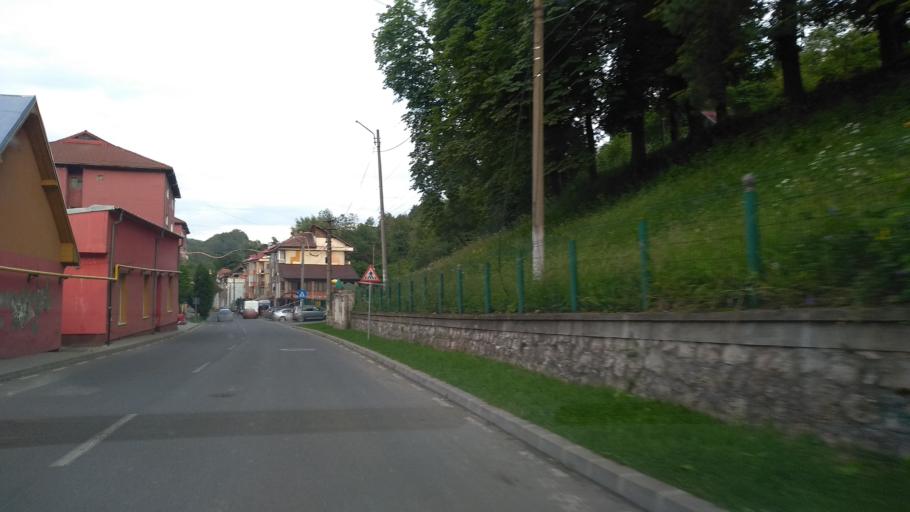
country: RO
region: Hunedoara
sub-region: Comuna Aninoasa
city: Aninoasa
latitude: 45.4095
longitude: 23.3132
